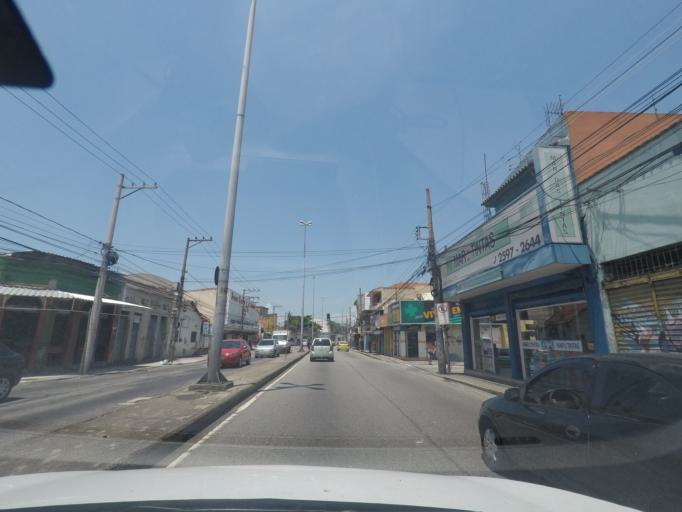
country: BR
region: Rio de Janeiro
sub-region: Rio De Janeiro
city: Rio de Janeiro
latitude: -22.8861
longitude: -43.3022
